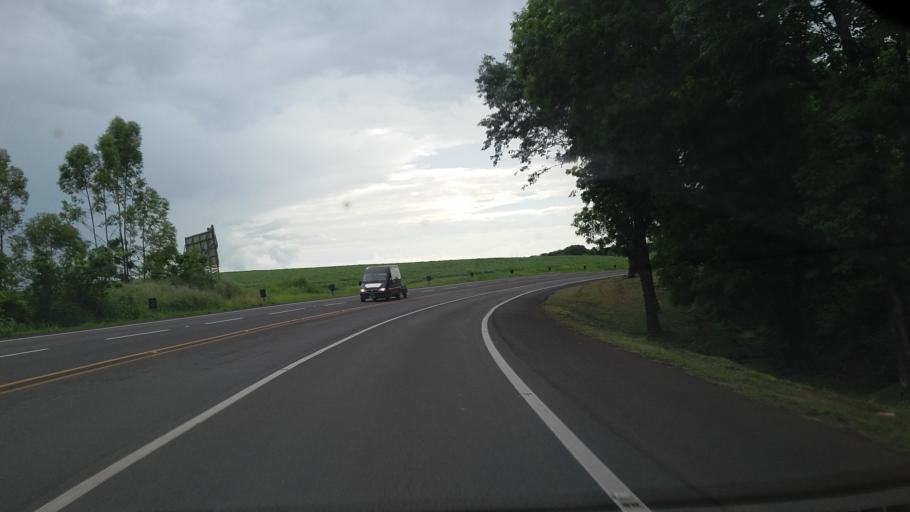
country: BR
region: Parana
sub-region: Arapongas
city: Arapongas
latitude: -23.4341
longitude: -51.5376
